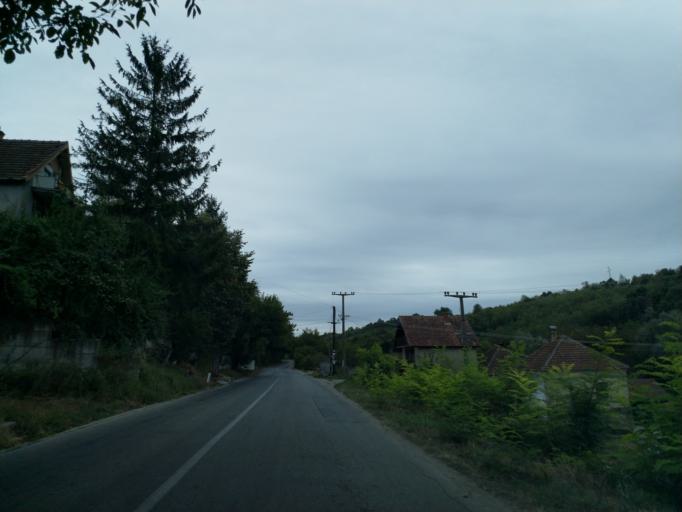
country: RS
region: Central Serbia
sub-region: Pomoravski Okrug
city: Jagodina
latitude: 44.0478
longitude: 21.1831
